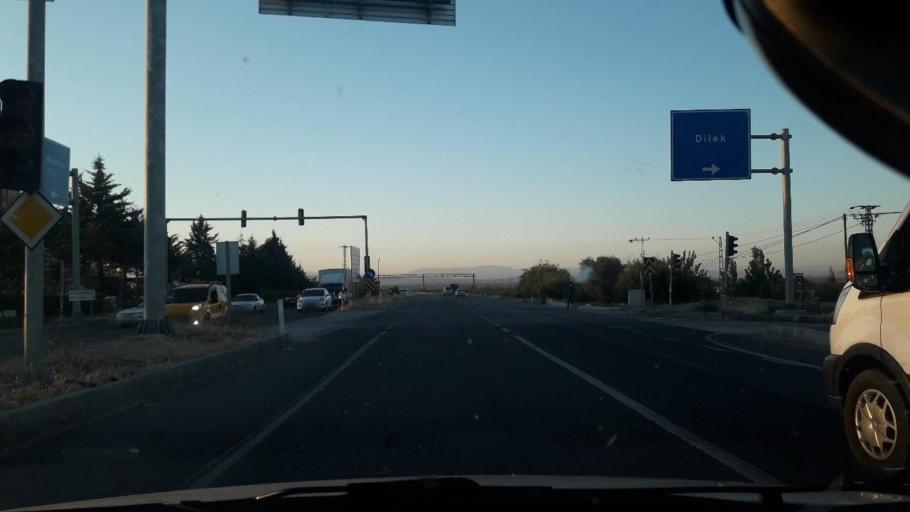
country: TR
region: Malatya
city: Malatya
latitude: 38.4479
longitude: 38.2269
